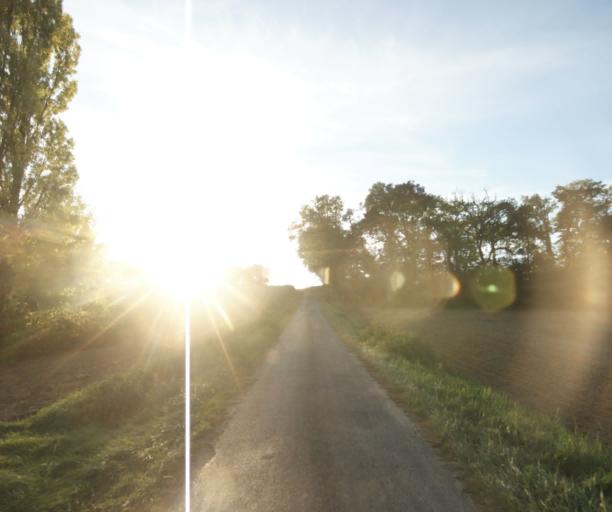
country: FR
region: Midi-Pyrenees
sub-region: Departement du Gers
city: Gondrin
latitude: 43.8613
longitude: 0.2778
